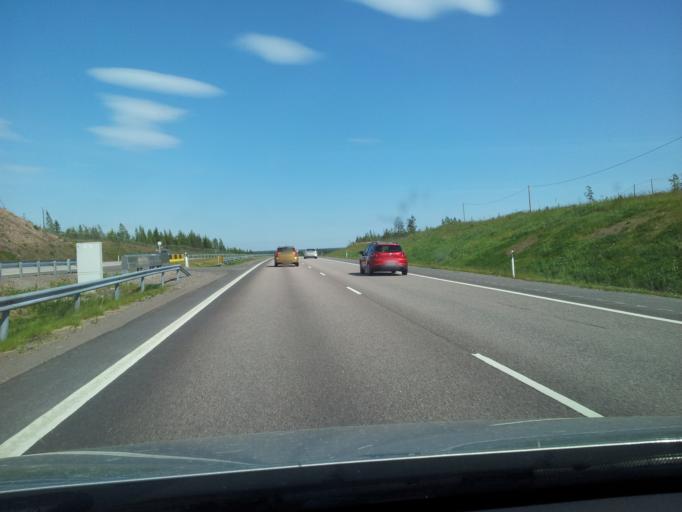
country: FI
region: Uusimaa
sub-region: Loviisa
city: Perna
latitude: 60.4785
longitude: 26.0882
